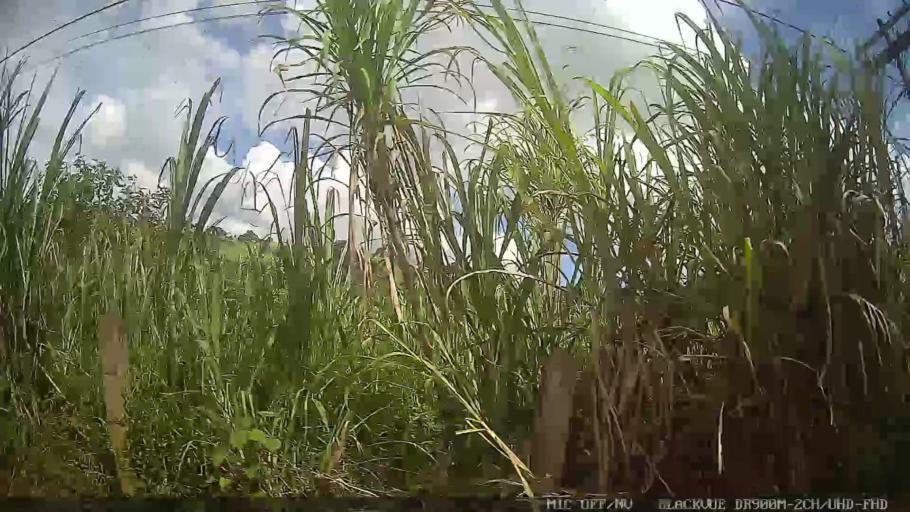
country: BR
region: Minas Gerais
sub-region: Extrema
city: Extrema
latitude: -22.8382
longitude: -46.2471
